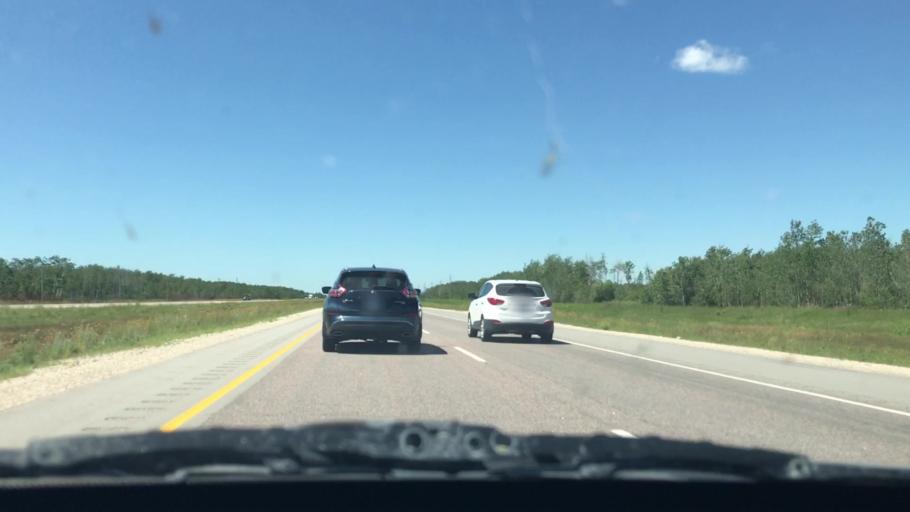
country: CA
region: Manitoba
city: La Broquerie
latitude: 49.6747
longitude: -96.5801
